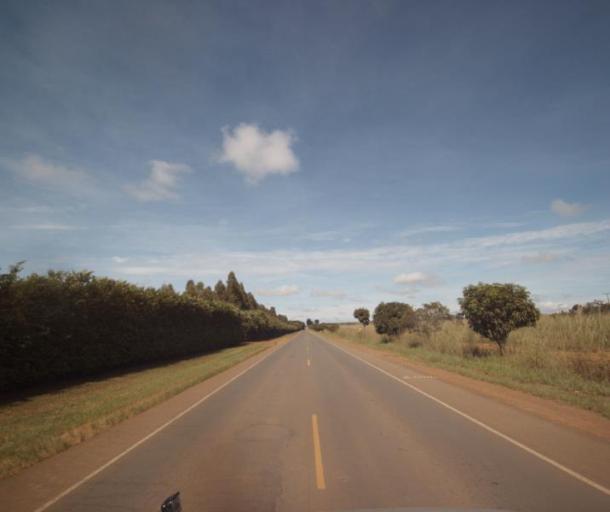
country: BR
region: Goias
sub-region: Anapolis
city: Anapolis
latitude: -16.2106
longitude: -48.9163
